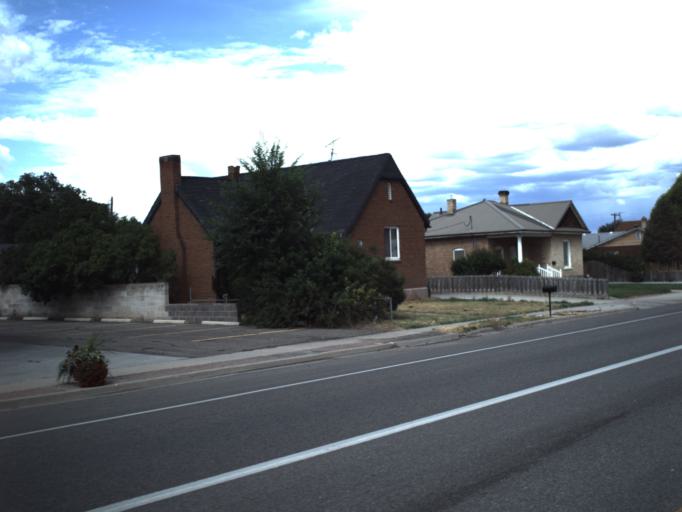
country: US
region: Utah
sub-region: Sevier County
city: Richfield
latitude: 38.7722
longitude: -112.0828
